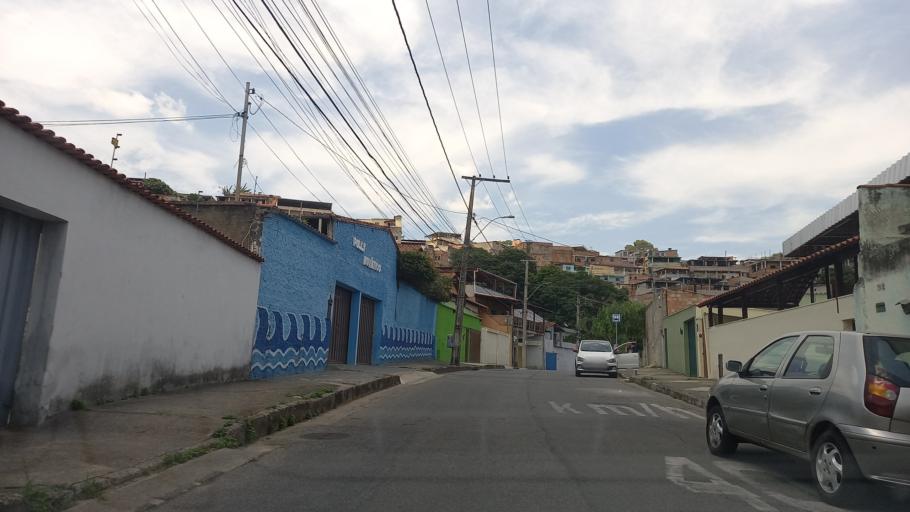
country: BR
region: Minas Gerais
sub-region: Contagem
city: Contagem
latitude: -19.9093
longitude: -44.0062
